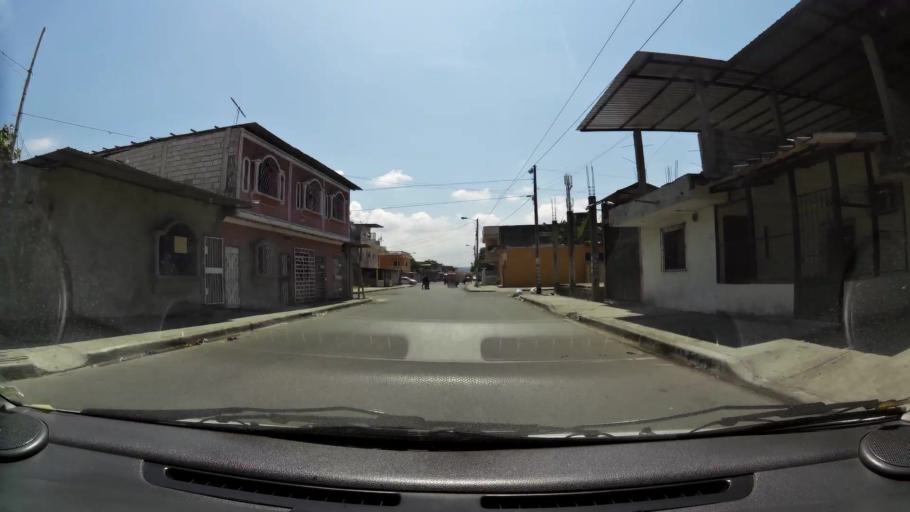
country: EC
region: Guayas
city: Guayaquil
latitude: -2.2351
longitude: -79.9194
